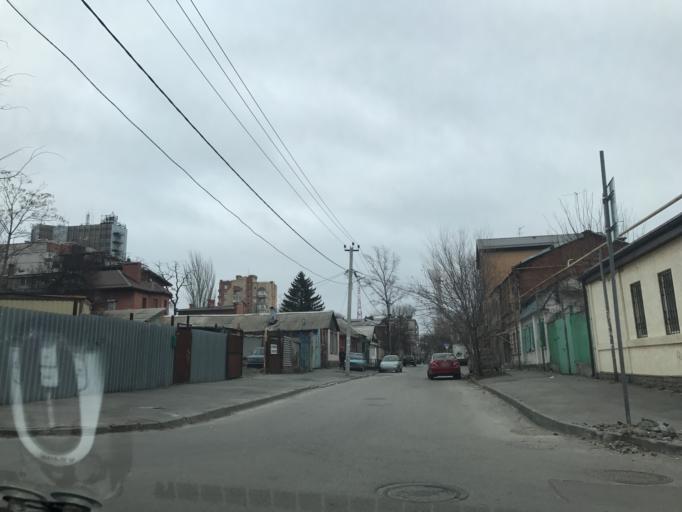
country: RU
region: Rostov
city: Rostov-na-Donu
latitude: 47.2248
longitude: 39.7403
